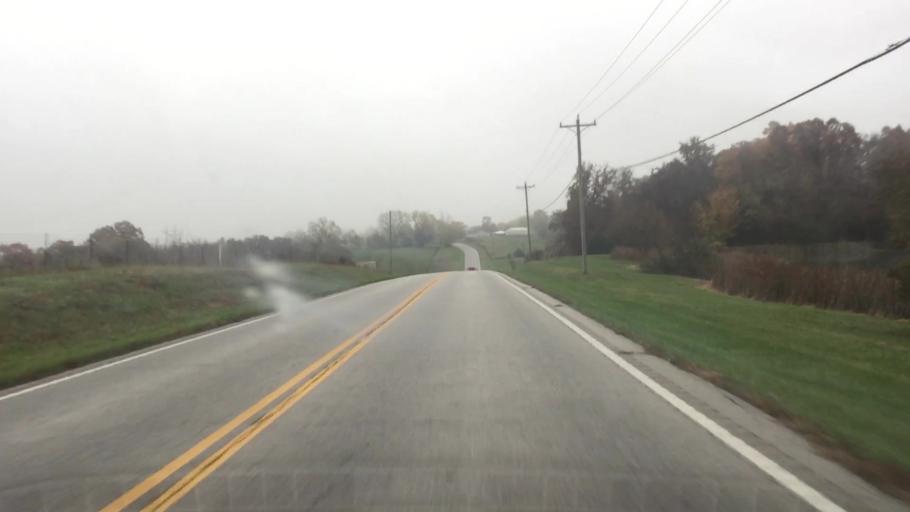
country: US
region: Missouri
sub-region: Callaway County
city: Fulton
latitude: 38.8612
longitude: -92.0025
